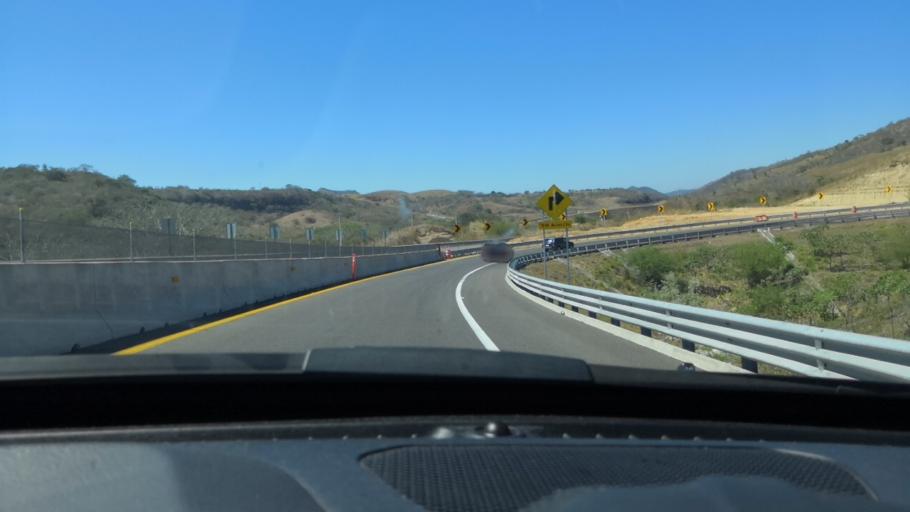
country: MX
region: Nayarit
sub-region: Compostela
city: Juan Escutia (Borbollon)
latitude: 21.1388
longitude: -104.9236
